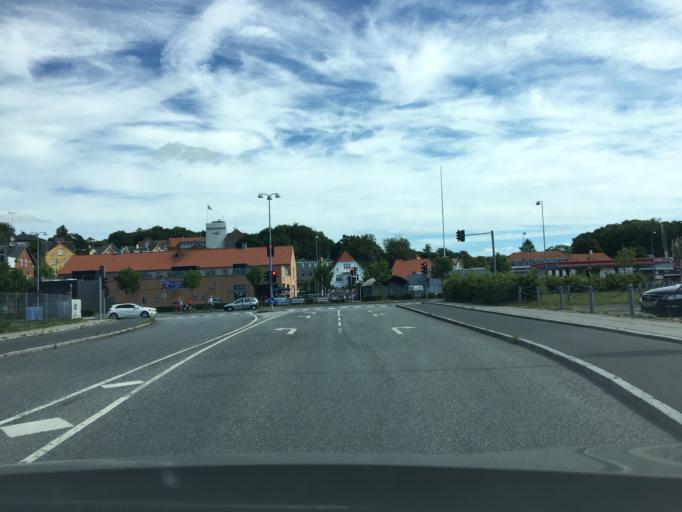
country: DK
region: South Denmark
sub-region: Svendborg Kommune
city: Svendborg
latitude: 55.0628
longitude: 10.6178
